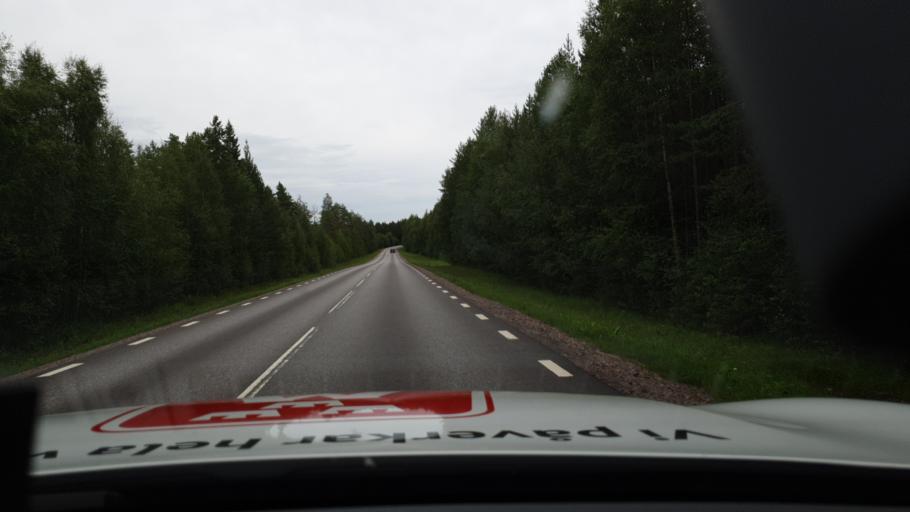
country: SE
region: Norrbotten
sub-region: Lulea Kommun
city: Gammelstad
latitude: 65.5246
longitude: 21.9655
